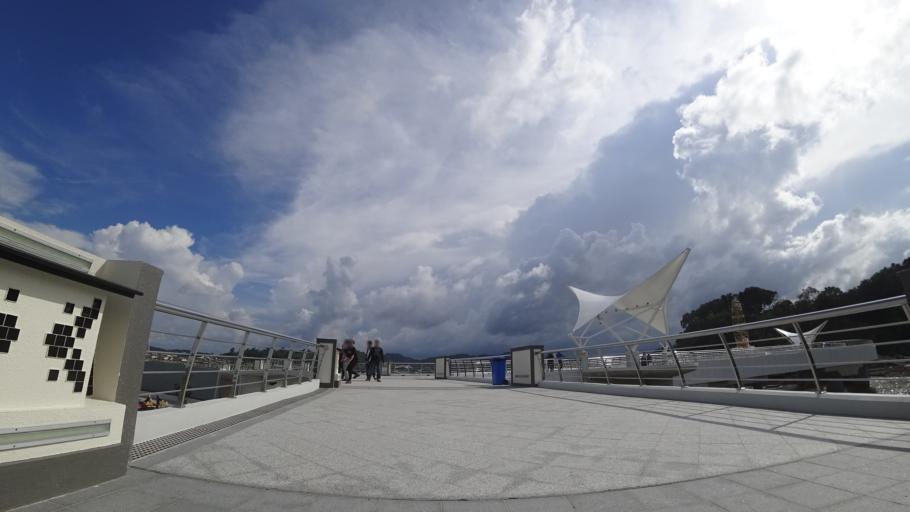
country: BN
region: Brunei and Muara
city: Bandar Seri Begawan
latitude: 4.8886
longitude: 114.9371
